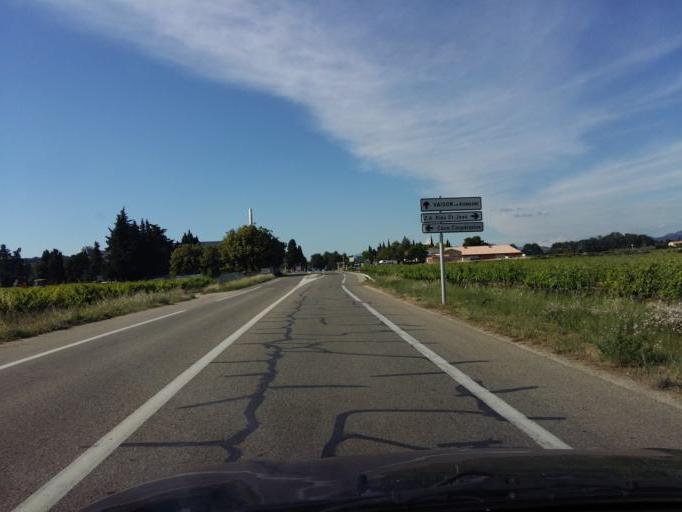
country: FR
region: Provence-Alpes-Cote d'Azur
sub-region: Departement du Vaucluse
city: Sablet
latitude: 44.2196
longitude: 5.0075
